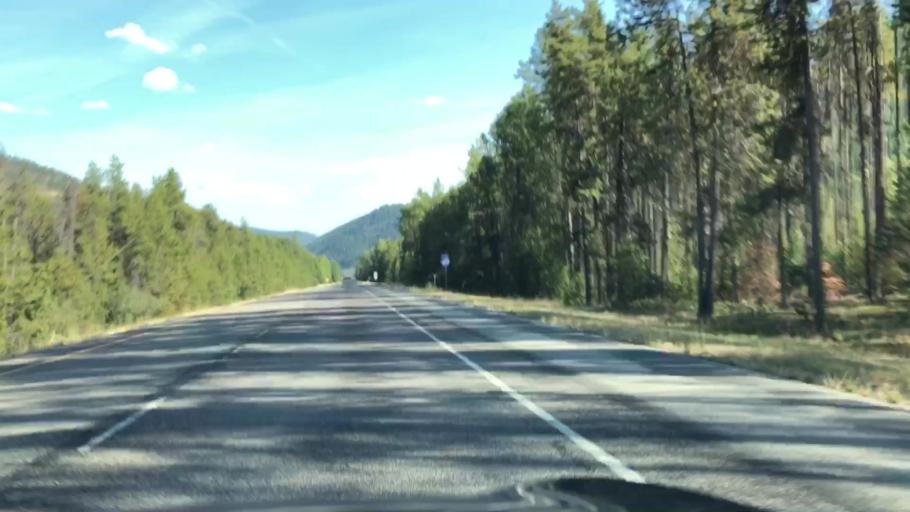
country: US
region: Montana
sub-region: Sanders County
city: Thompson Falls
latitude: 47.3720
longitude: -115.3423
